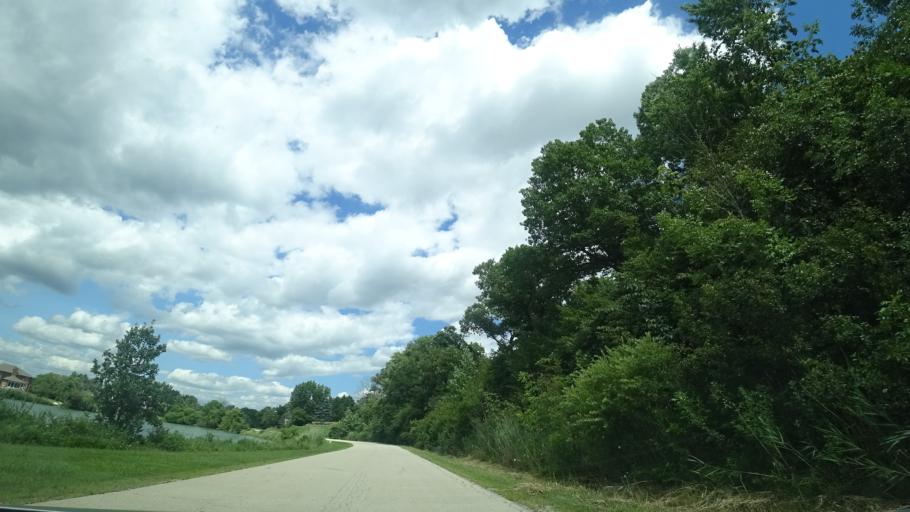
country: US
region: Illinois
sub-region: Will County
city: Homer Glen
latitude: 41.5890
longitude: -87.9161
